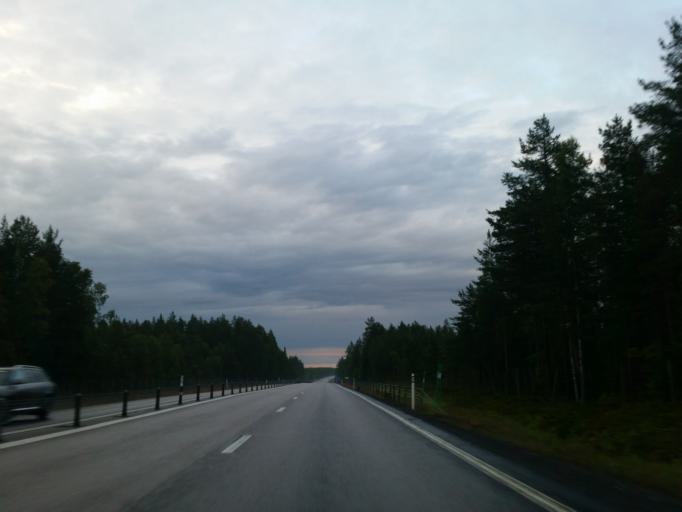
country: SE
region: Vaesterbotten
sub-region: Umea Kommun
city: Saevar
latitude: 63.9759
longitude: 20.7194
